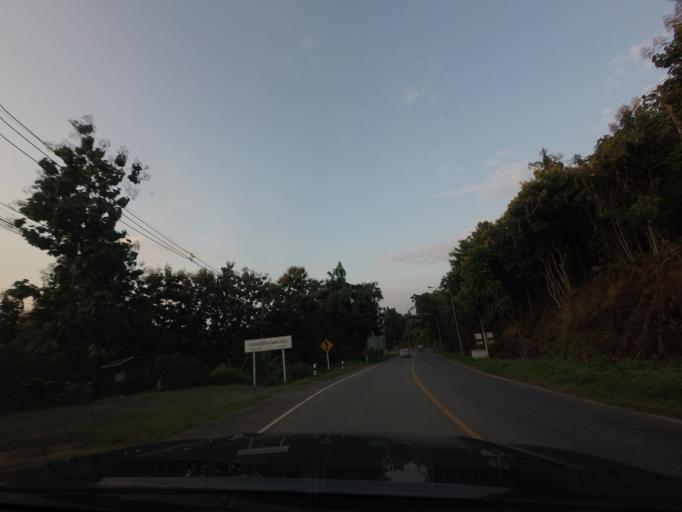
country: TH
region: Nan
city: Na Noi
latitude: 18.3705
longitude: 100.7055
